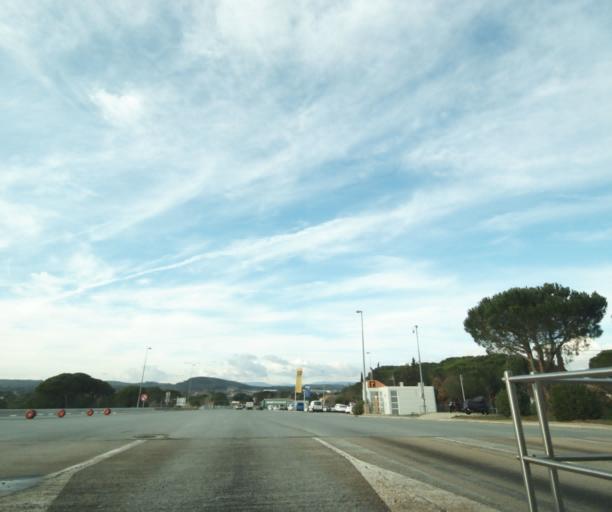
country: FR
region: Provence-Alpes-Cote d'Azur
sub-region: Departement du Var
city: Le Muy
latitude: 43.4609
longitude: 6.5509
